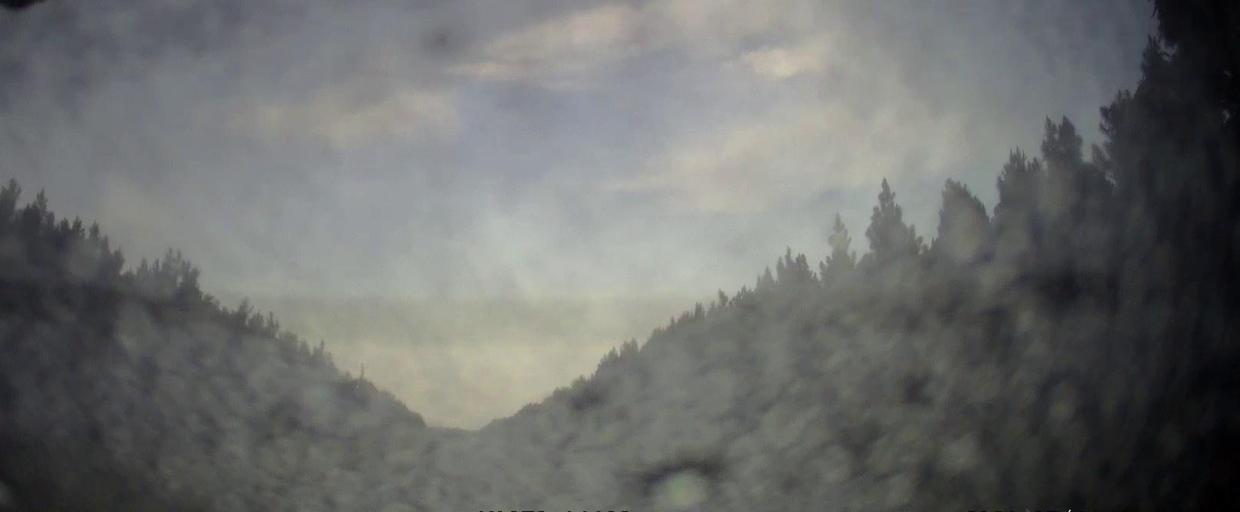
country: US
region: Georgia
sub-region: Dodge County
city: Chester
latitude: 32.5493
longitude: -83.1274
